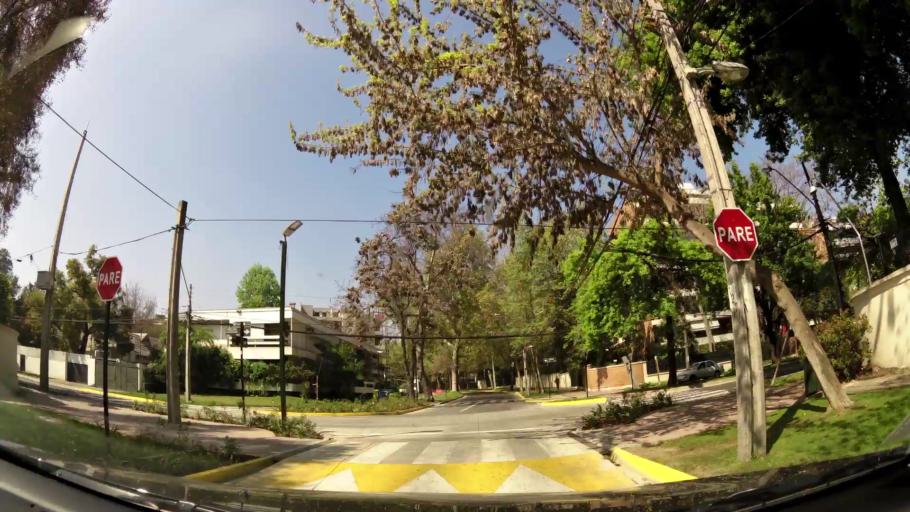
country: CL
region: Santiago Metropolitan
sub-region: Provincia de Santiago
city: Villa Presidente Frei, Nunoa, Santiago, Chile
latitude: -33.3977
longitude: -70.5928
